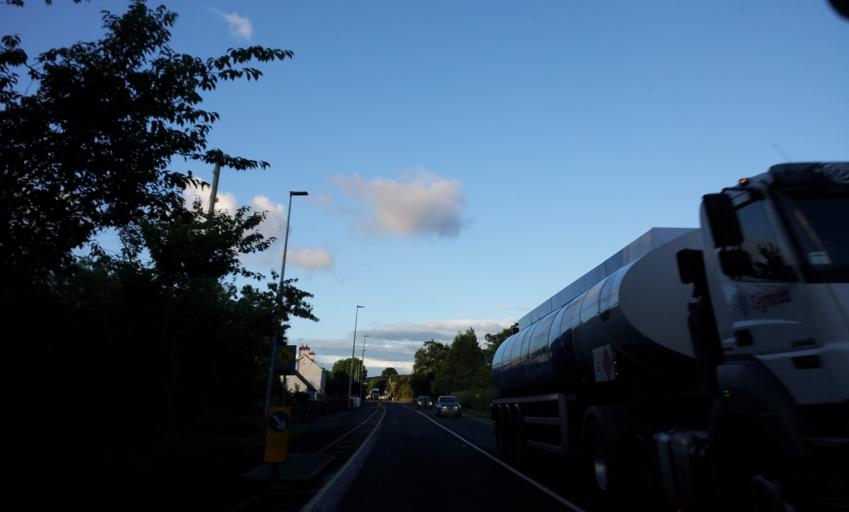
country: IE
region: Munster
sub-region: County Limerick
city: Abbeyfeale
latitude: 52.3933
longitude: -9.1824
